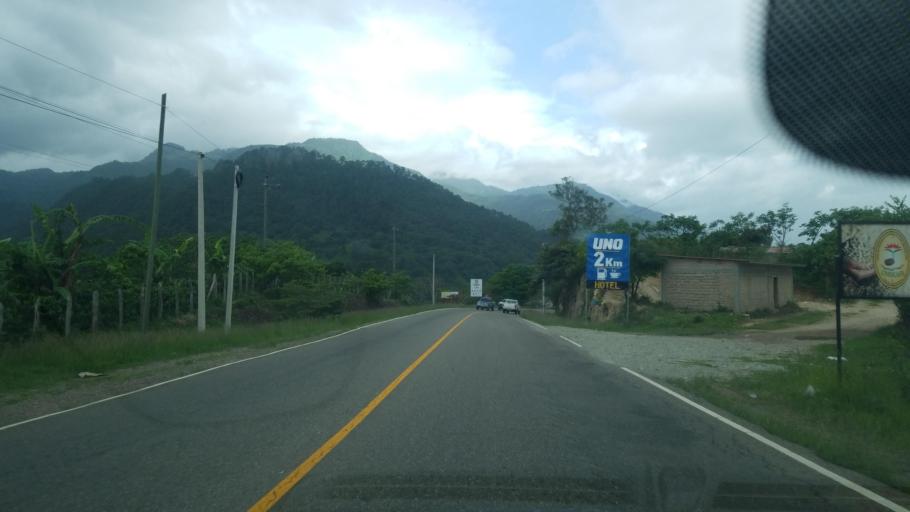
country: HN
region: Ocotepeque
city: Sinuapa
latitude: 14.4566
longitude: -89.1703
